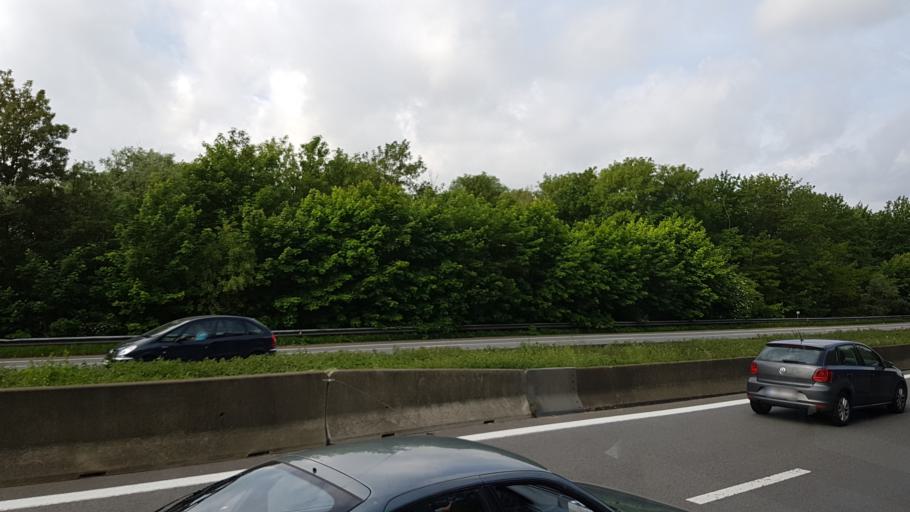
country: BE
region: Flanders
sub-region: Provincie Vlaams-Brabant
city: Oud-Heverlee
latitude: 50.8509
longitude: 4.6674
